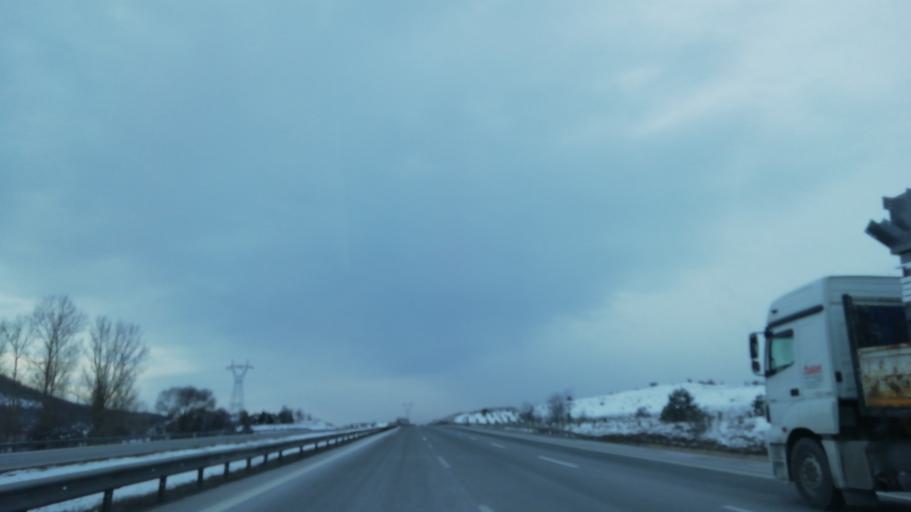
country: TR
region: Bolu
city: Yenicaga
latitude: 40.7620
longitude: 31.9863
